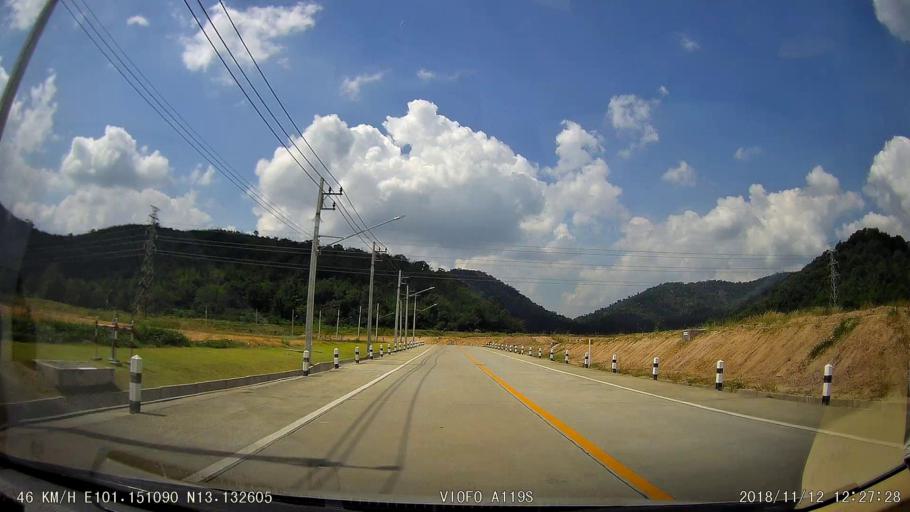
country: TH
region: Chon Buri
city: Ban Talat Bueng
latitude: 13.1327
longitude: 101.1506
